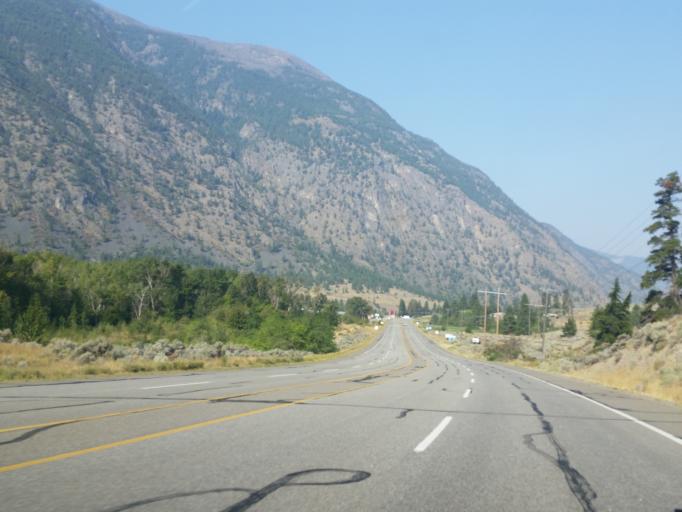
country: CA
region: British Columbia
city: Oliver
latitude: 49.2054
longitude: -119.8724
